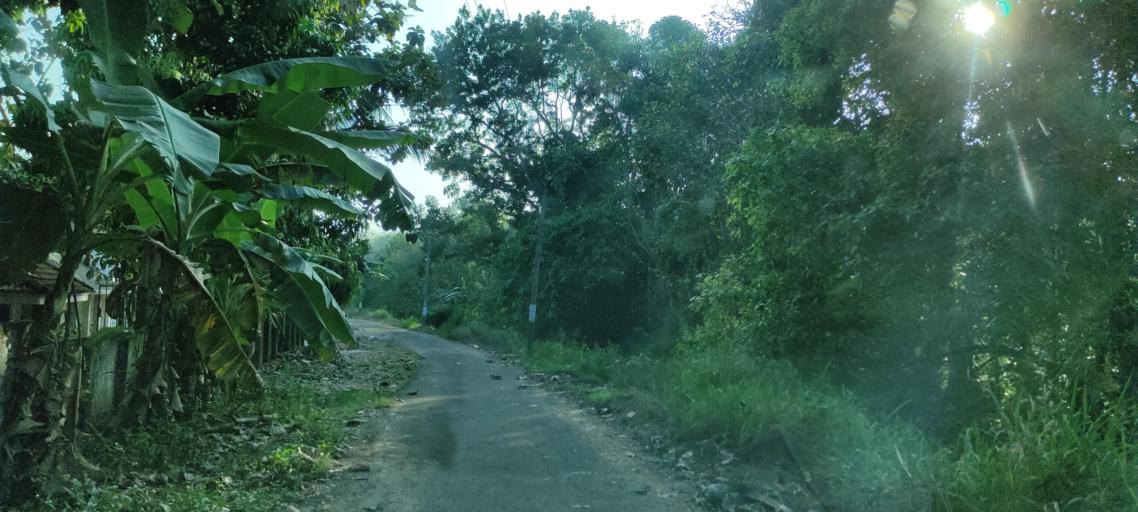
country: IN
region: Kerala
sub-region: Pattanamtitta
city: Adur
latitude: 9.1407
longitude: 76.7324
